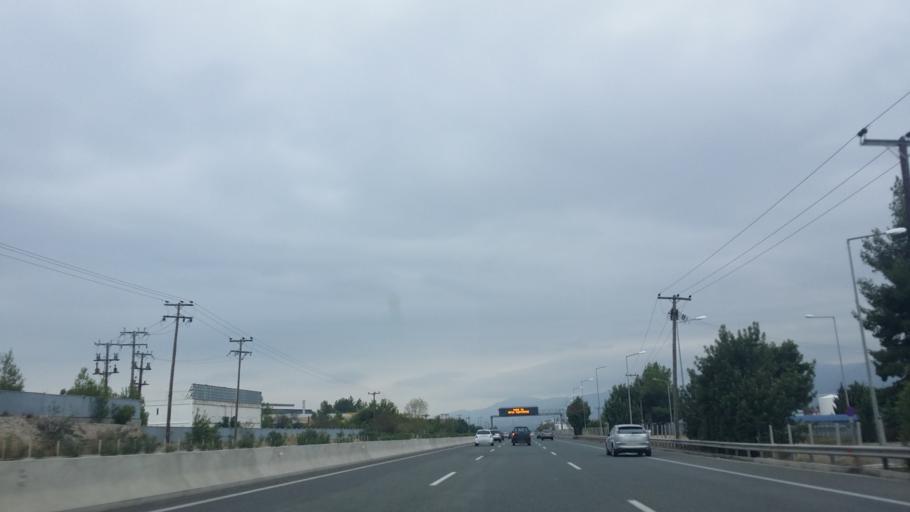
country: GR
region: Central Greece
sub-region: Nomos Voiotias
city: Oinofyta
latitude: 38.3176
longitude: 23.6269
